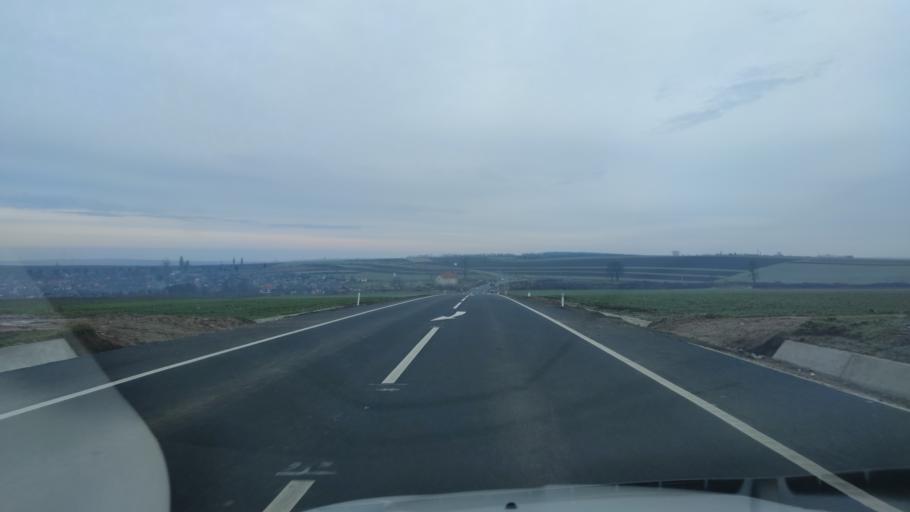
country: RO
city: Szekelyhid
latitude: 47.3436
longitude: 22.1208
